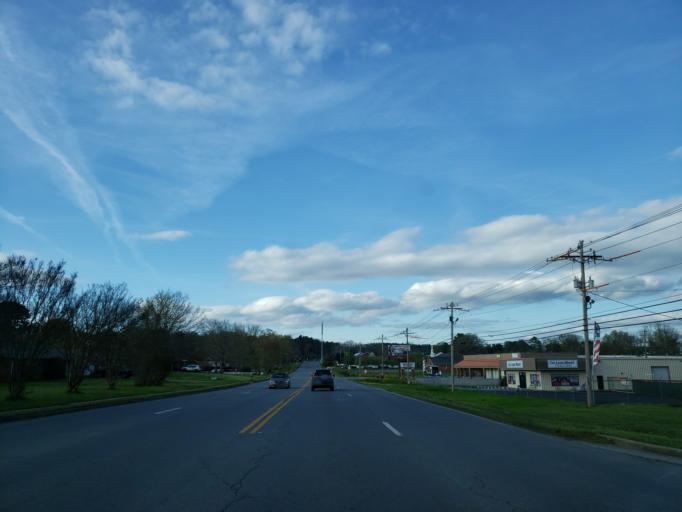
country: US
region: Georgia
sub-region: Bartow County
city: Cartersville
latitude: 34.2197
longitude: -84.8189
